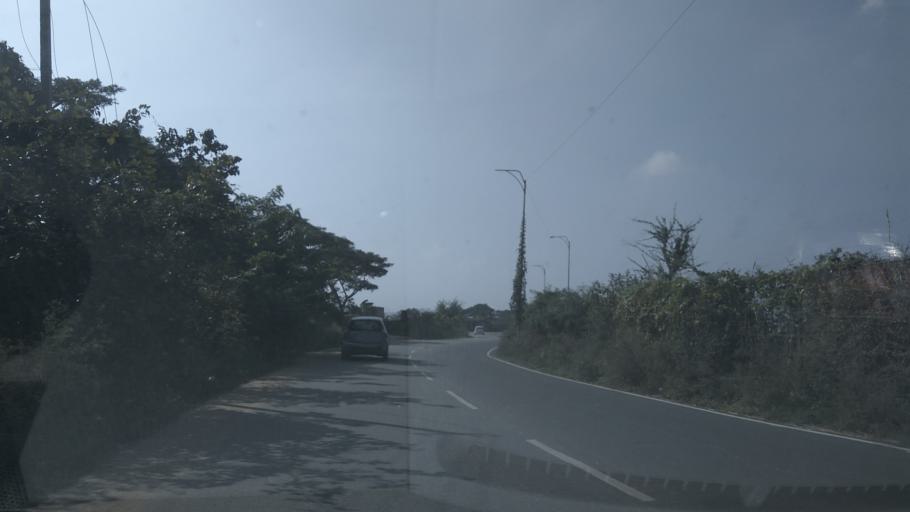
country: IN
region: Karnataka
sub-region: Bangalore Urban
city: Bangalore
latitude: 12.9405
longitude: 77.6787
